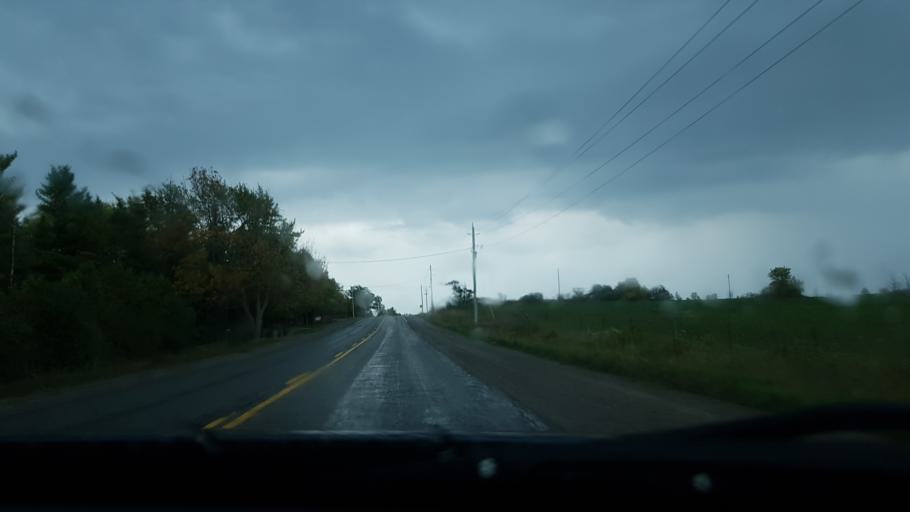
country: CA
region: Ontario
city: Omemee
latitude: 44.3660
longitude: -78.5443
